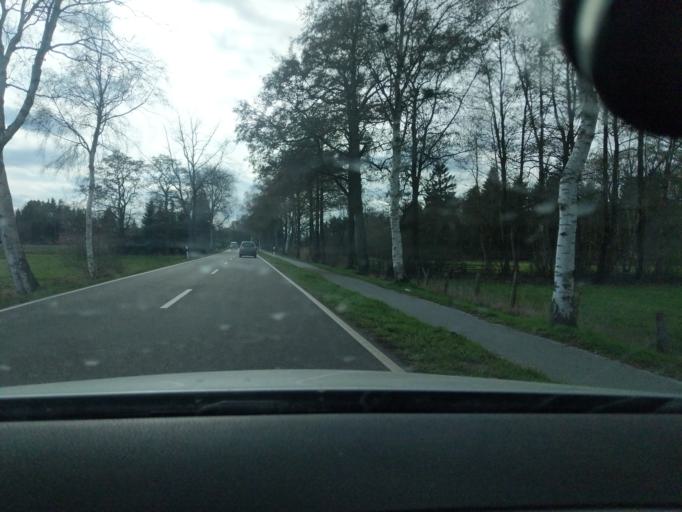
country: DE
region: Lower Saxony
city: Himmelpforten
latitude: 53.6348
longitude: 9.3243
